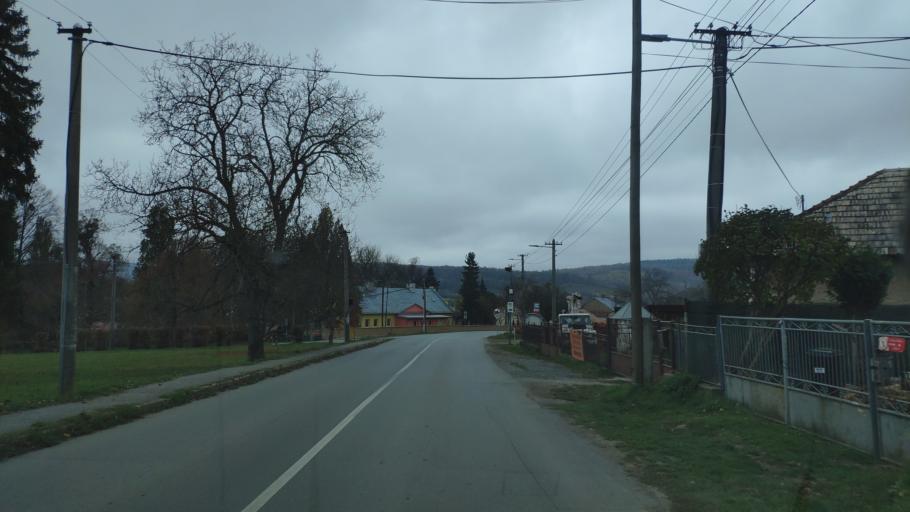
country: SK
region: Presovsky
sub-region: Okres Presov
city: Presov
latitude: 49.0129
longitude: 21.1859
